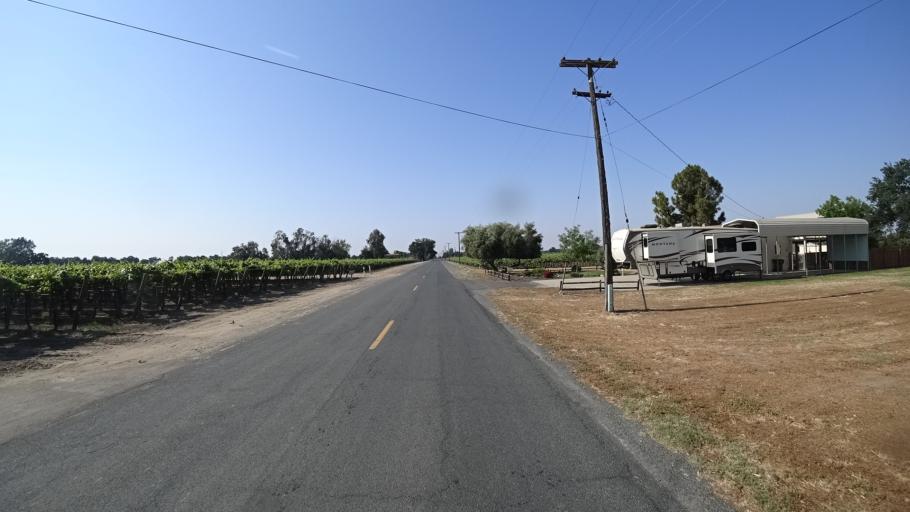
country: US
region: California
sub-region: Kings County
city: Lemoore
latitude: 36.3482
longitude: -119.8340
